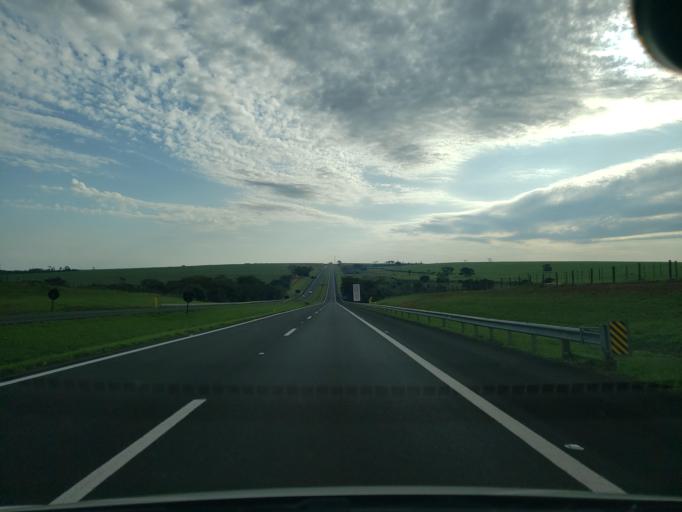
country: BR
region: Sao Paulo
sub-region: Guararapes
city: Guararapes
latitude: -21.2096
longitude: -50.7375
